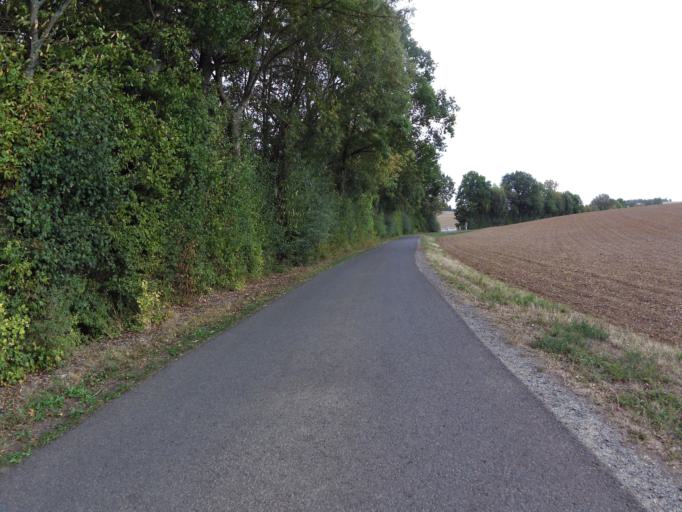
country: DE
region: Bavaria
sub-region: Regierungsbezirk Unterfranken
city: Eisingen
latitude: 49.7717
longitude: 9.8170
